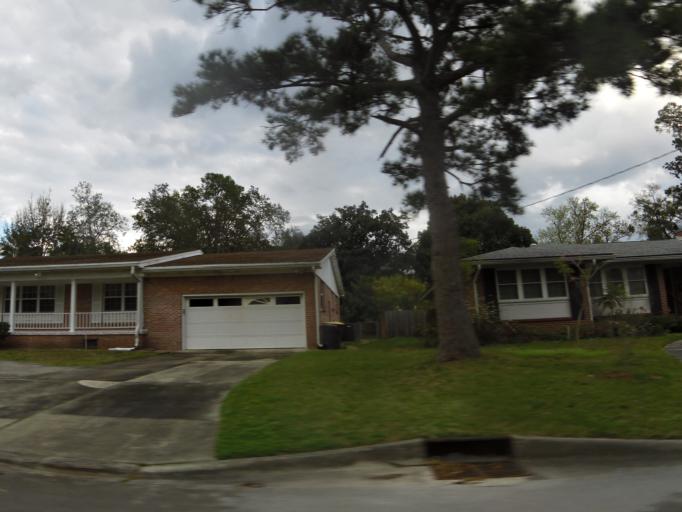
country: US
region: Florida
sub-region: Duval County
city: Jacksonville
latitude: 30.2508
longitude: -81.6356
